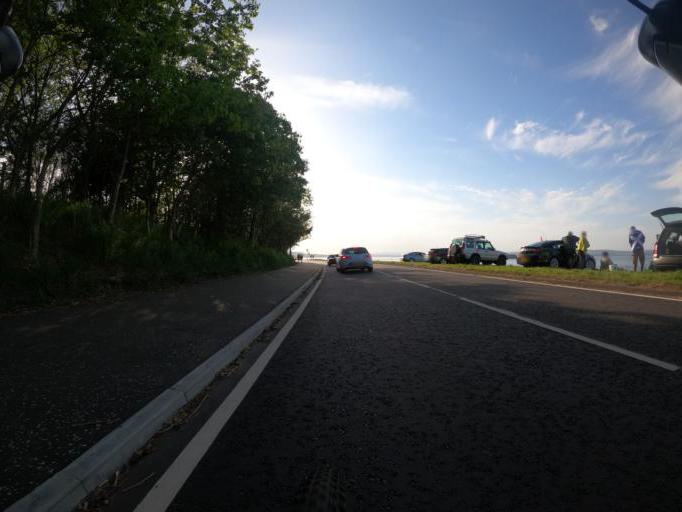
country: GB
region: Scotland
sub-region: Edinburgh
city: Colinton
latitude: 55.9791
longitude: -3.2740
